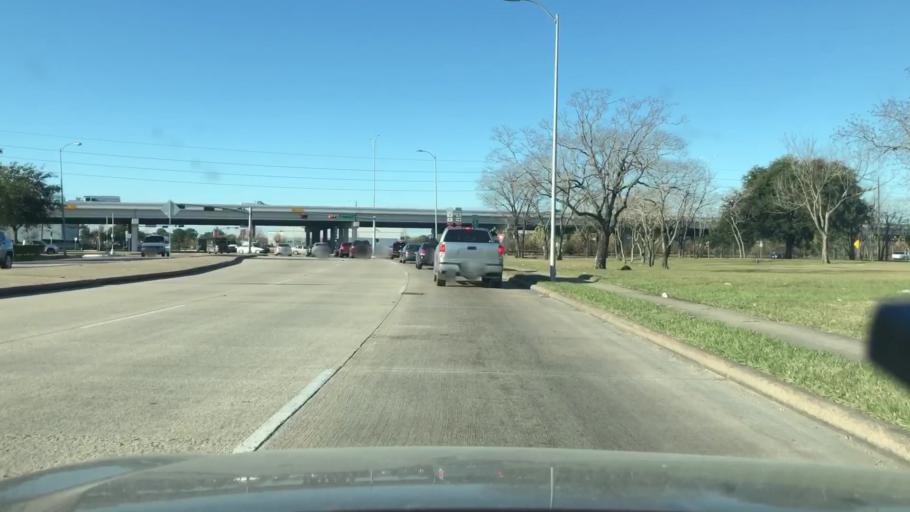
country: US
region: Texas
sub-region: Fort Bend County
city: Missouri City
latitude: 29.6451
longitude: -95.5378
